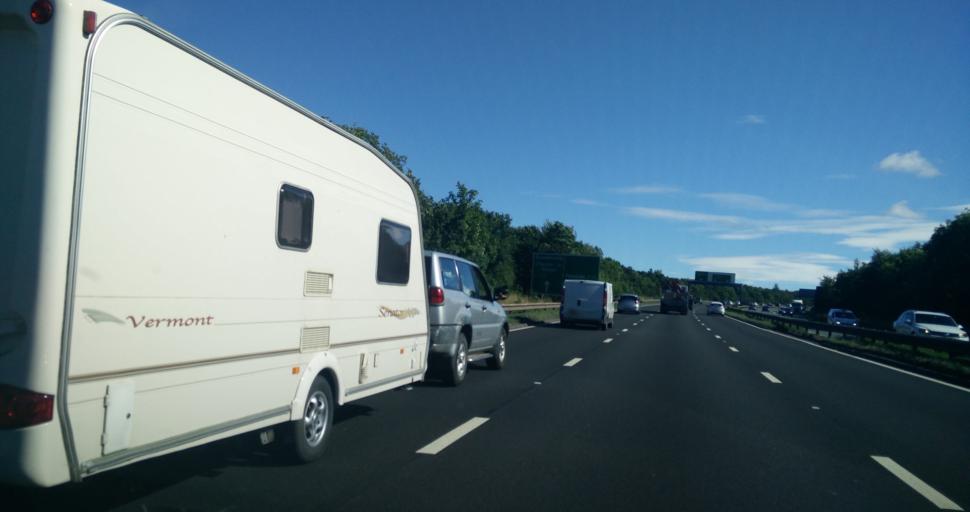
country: GB
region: England
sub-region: South Tyneside
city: The Boldons
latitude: 54.9028
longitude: -1.4570
